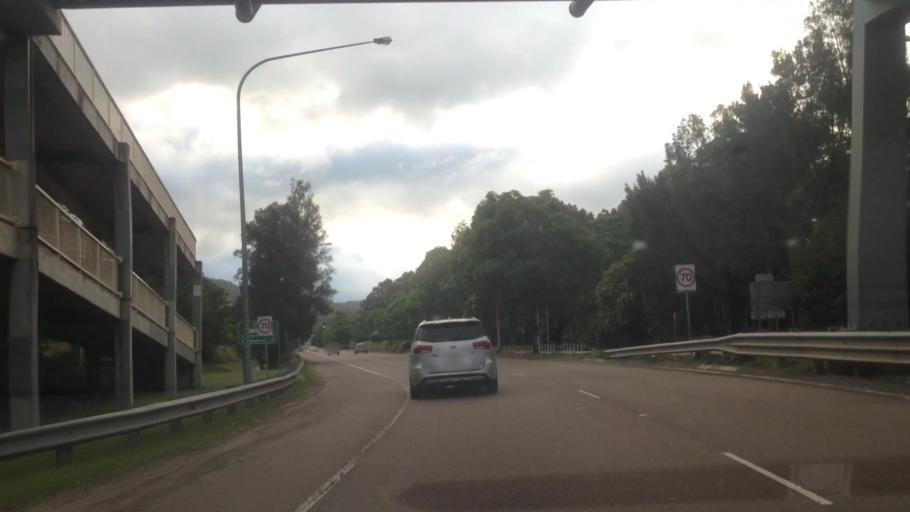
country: AU
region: New South Wales
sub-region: Wyong Shire
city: Chittaway Bay
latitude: -33.3069
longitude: 151.4149
